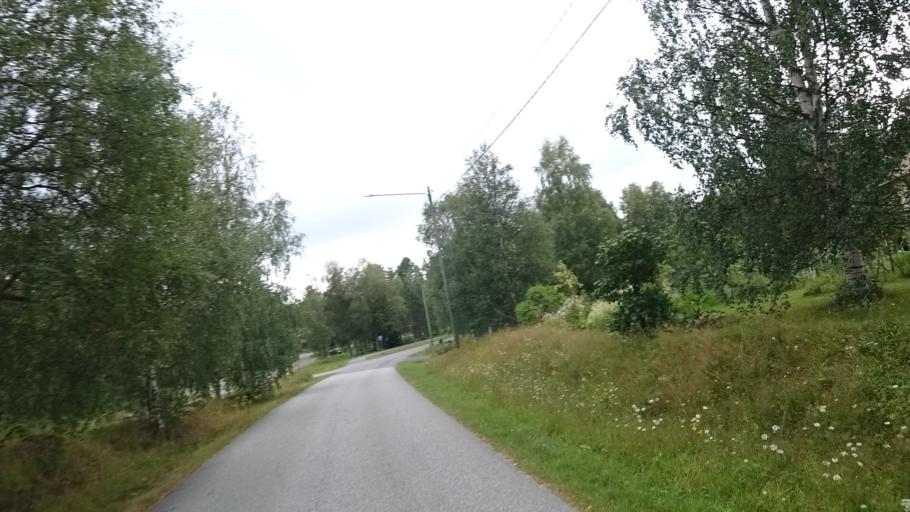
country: FI
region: North Karelia
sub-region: Joensuu
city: Ilomantsi
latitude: 62.6815
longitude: 30.9187
